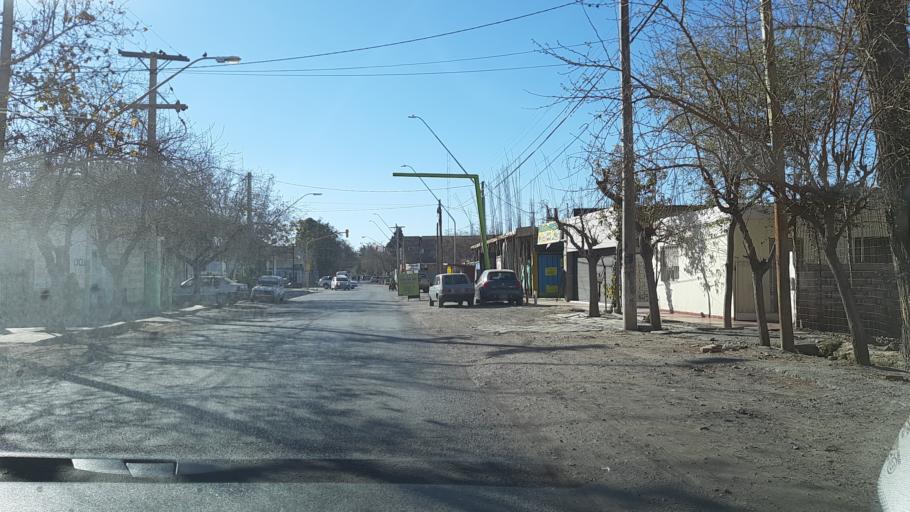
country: AR
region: San Juan
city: San Juan
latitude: -31.5397
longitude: -68.5671
